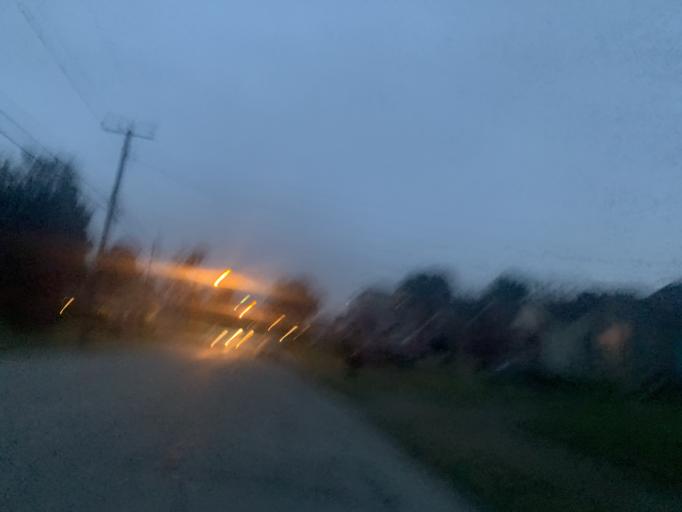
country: US
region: Kentucky
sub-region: Jefferson County
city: Louisville
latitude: 38.2147
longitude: -85.7679
